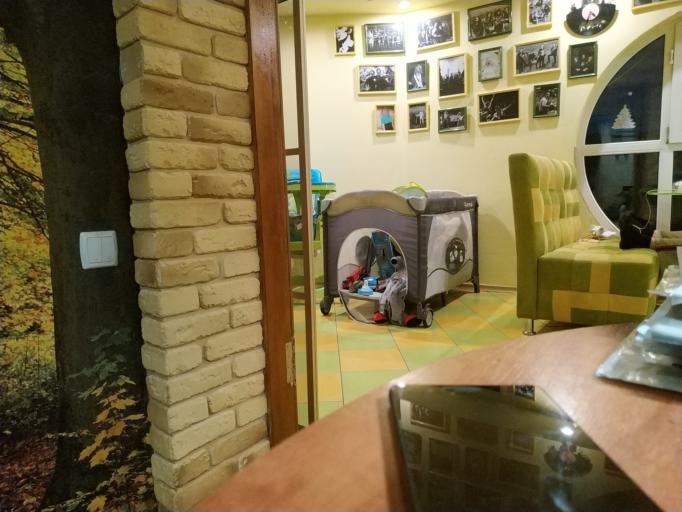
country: RU
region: Orjol
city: Znamenskoye
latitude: 53.1381
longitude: 35.6448
